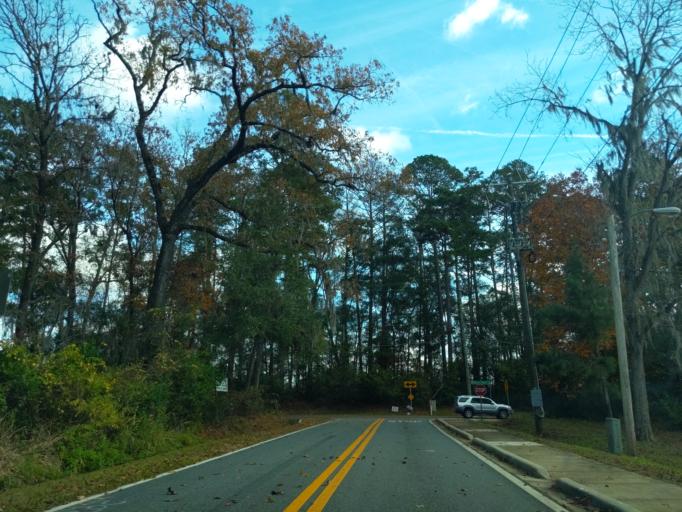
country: US
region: Florida
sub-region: Leon County
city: Tallahassee
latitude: 30.4685
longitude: -84.2108
